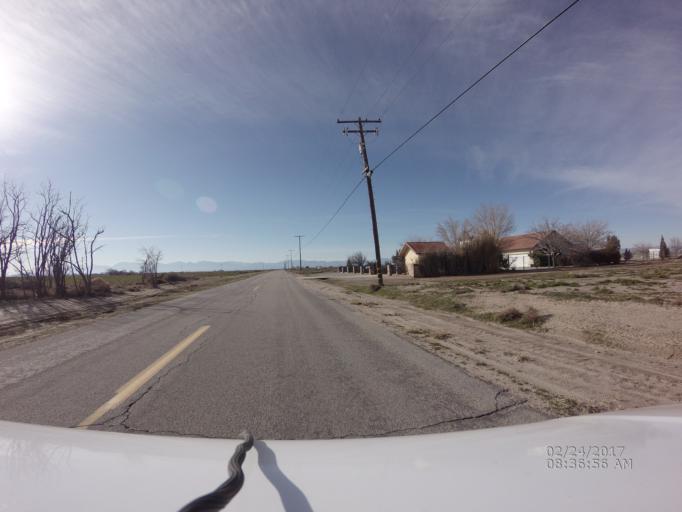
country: US
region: California
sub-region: Los Angeles County
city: Lancaster
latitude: 34.7377
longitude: -118.0233
